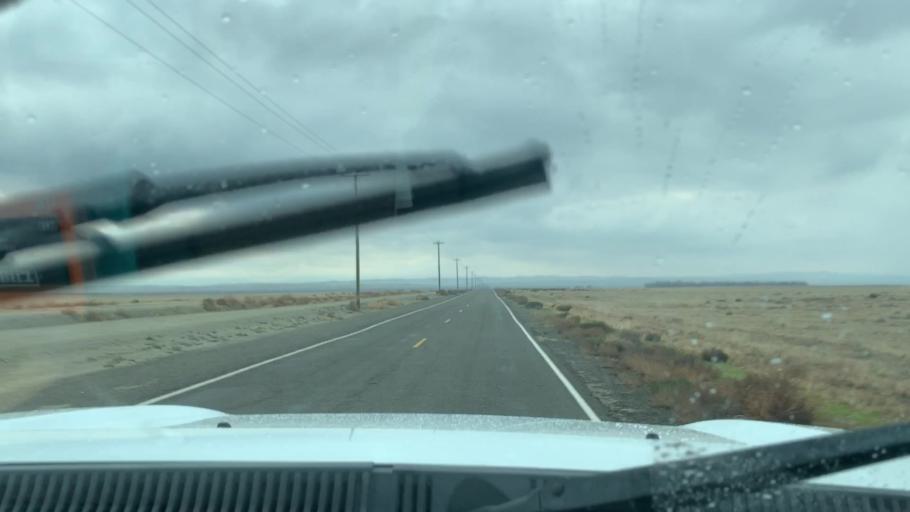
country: US
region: California
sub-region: Kings County
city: Kettleman City
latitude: 35.9341
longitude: -119.8461
